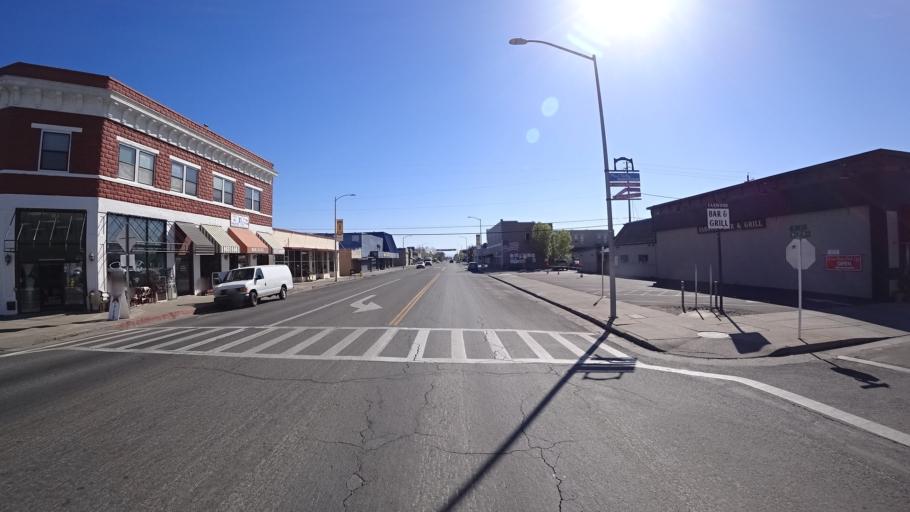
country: US
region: California
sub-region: Glenn County
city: Orland
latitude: 39.7474
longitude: -122.1954
